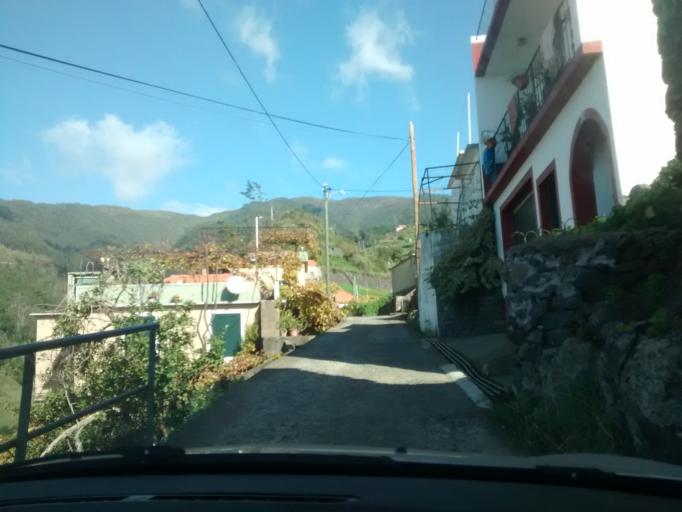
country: PT
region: Madeira
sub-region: Calheta
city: Arco da Calheta
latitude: 32.7314
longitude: -17.1597
